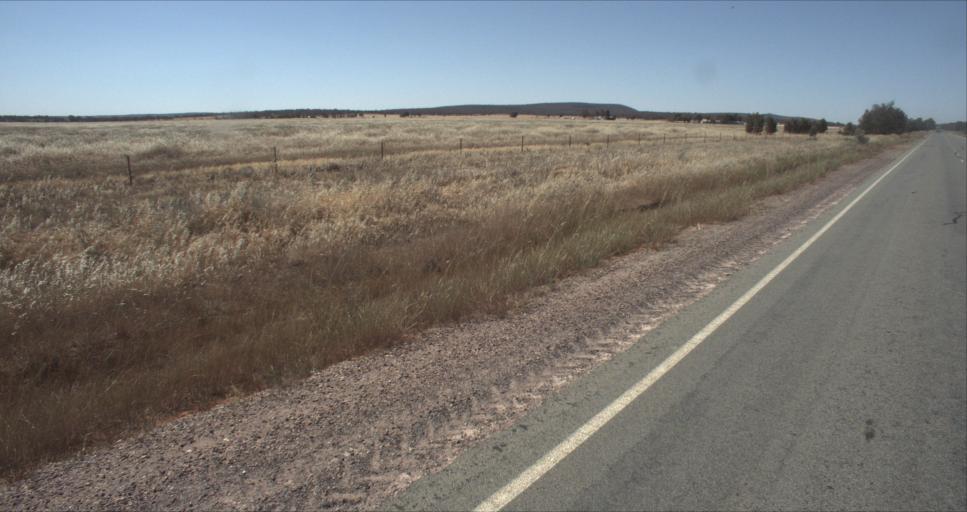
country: AU
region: New South Wales
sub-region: Leeton
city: Leeton
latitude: -34.5032
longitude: 146.4440
